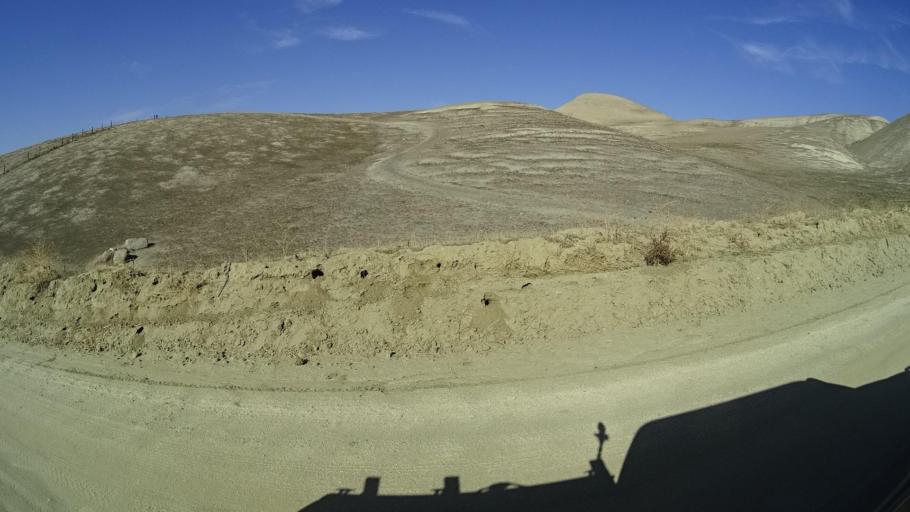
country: US
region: California
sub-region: Kern County
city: Oildale
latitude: 35.4818
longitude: -118.8229
